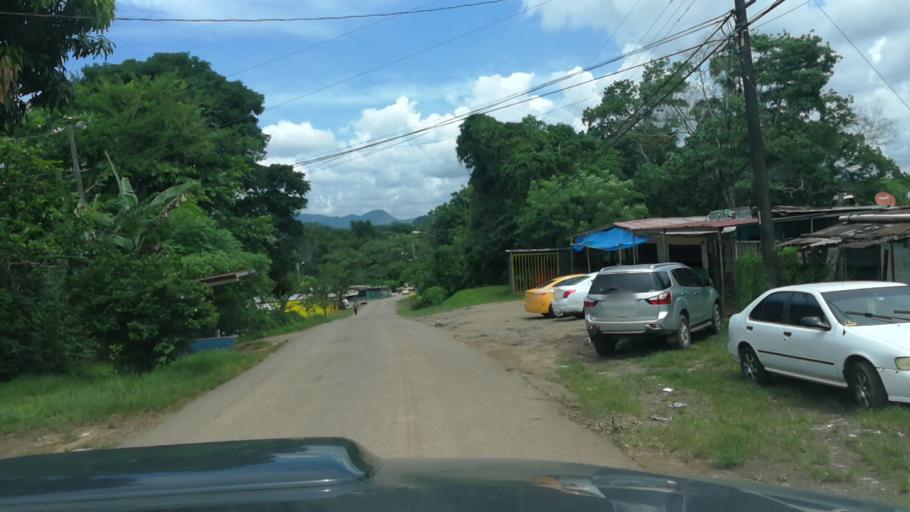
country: PA
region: Panama
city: San Miguelito
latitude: 9.0979
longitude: -79.4586
